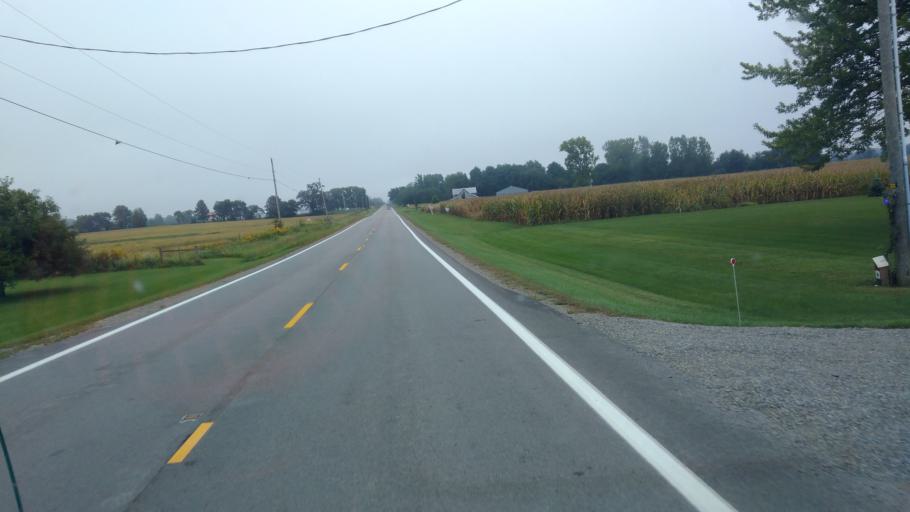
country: US
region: Ohio
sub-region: Union County
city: Richwood
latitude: 40.4799
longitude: -83.4773
